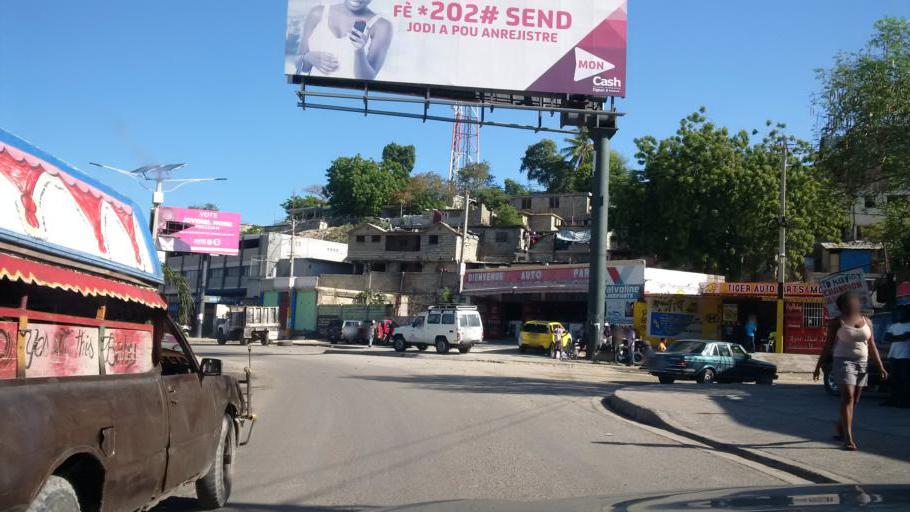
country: HT
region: Ouest
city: Delmas 73
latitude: 18.5558
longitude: -72.3144
